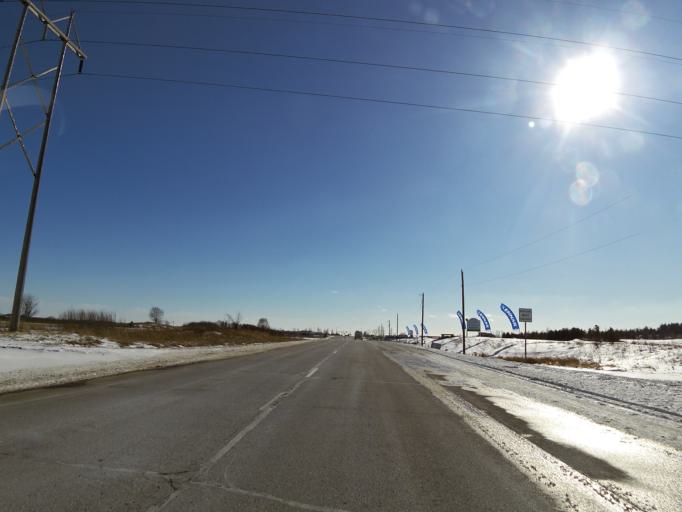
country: US
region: Minnesota
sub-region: Washington County
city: Lake Elmo
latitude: 44.9565
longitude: -92.9035
